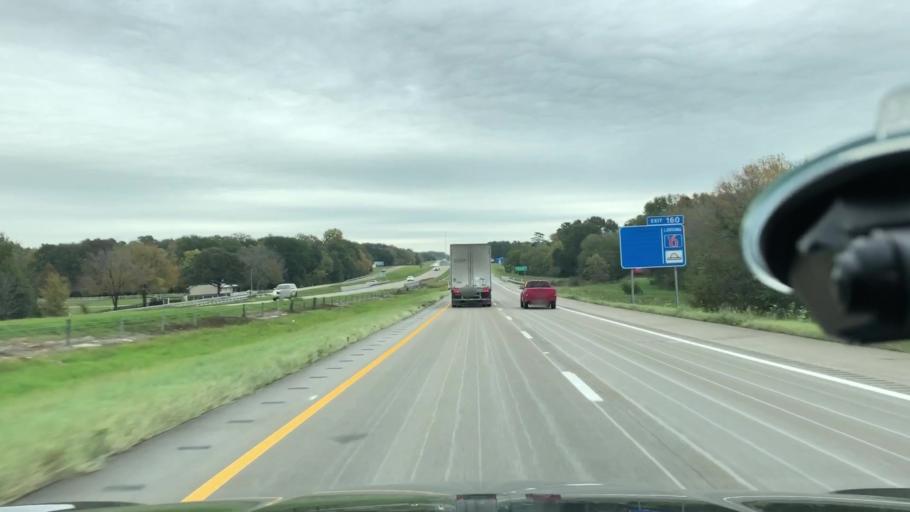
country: US
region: Texas
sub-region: Titus County
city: Mount Pleasant
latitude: 33.1641
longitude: -95.0175
